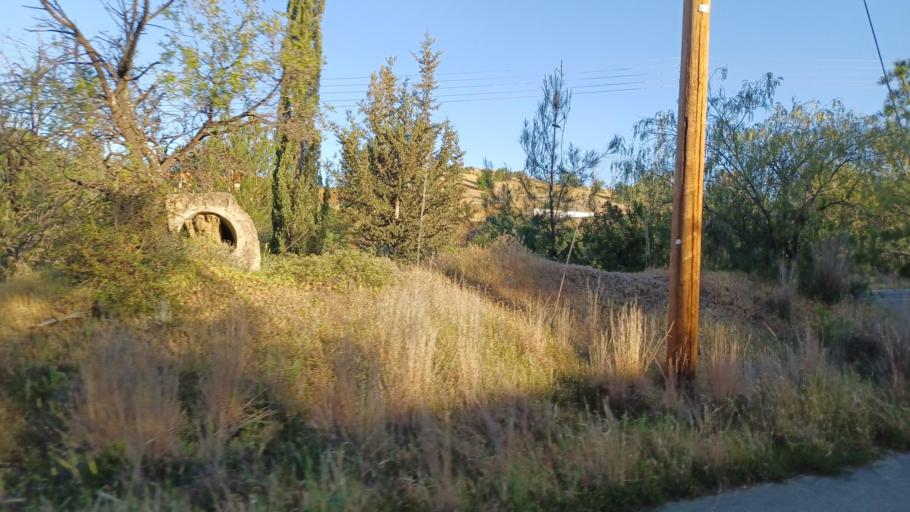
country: CY
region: Lefkosia
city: Peristerona
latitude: 35.0334
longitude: 33.0479
